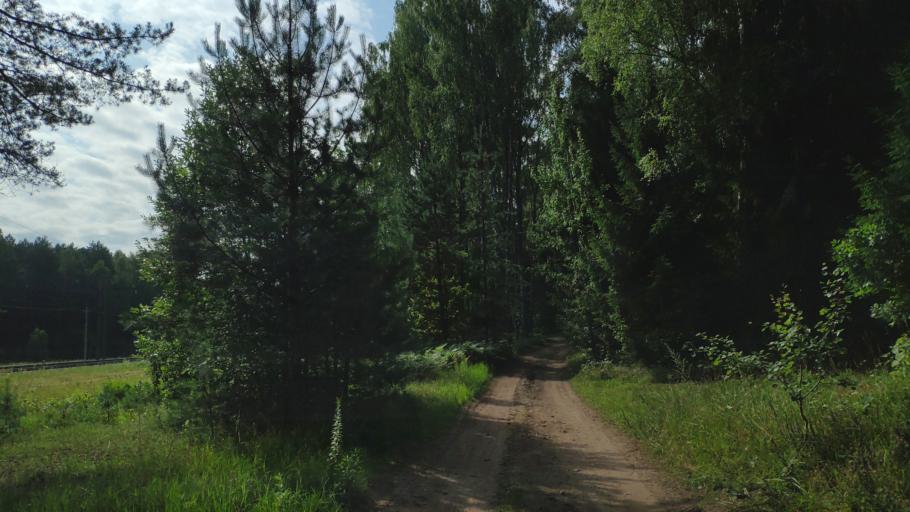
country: BY
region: Minsk
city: Zaslawye
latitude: 53.9675
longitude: 27.2963
